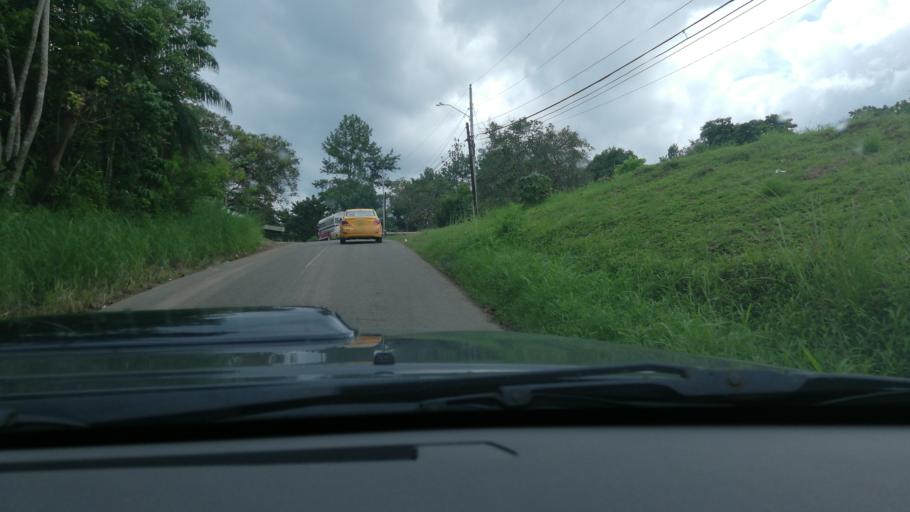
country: PA
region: Panama
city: San Miguelito
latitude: 9.0937
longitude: -79.4502
